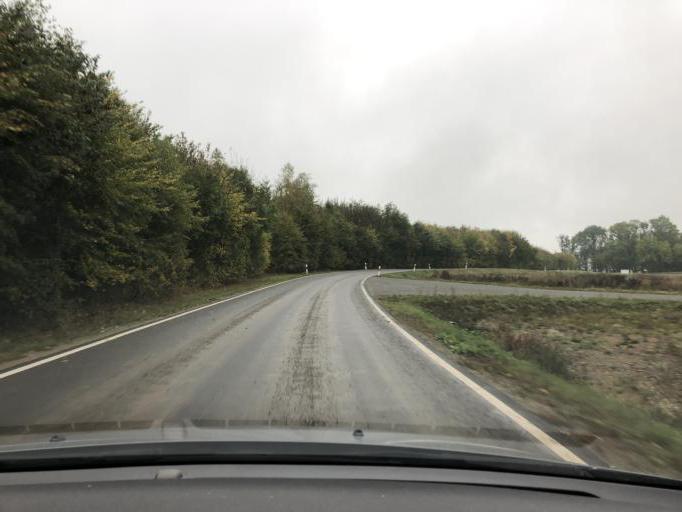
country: DE
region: Thuringia
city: Kreuzebra
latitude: 51.3611
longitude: 10.2640
